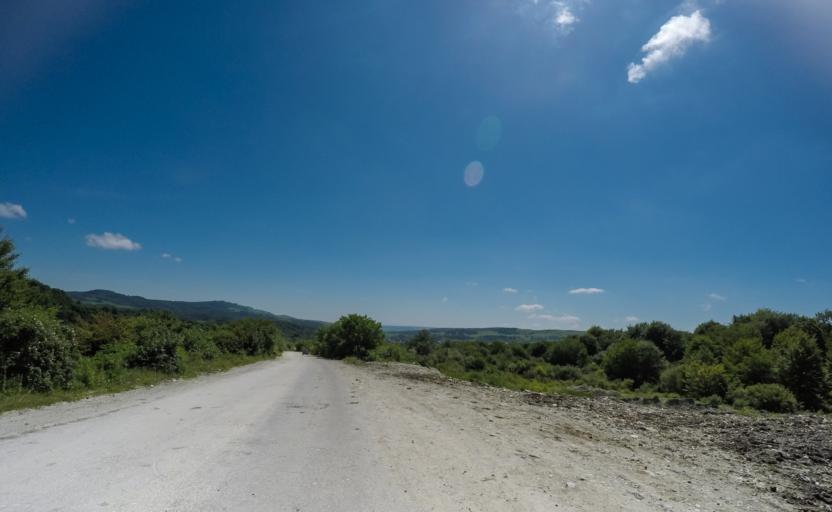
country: RU
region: Kabardino-Balkariya
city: Kashkhatau
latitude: 43.3716
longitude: 43.6231
